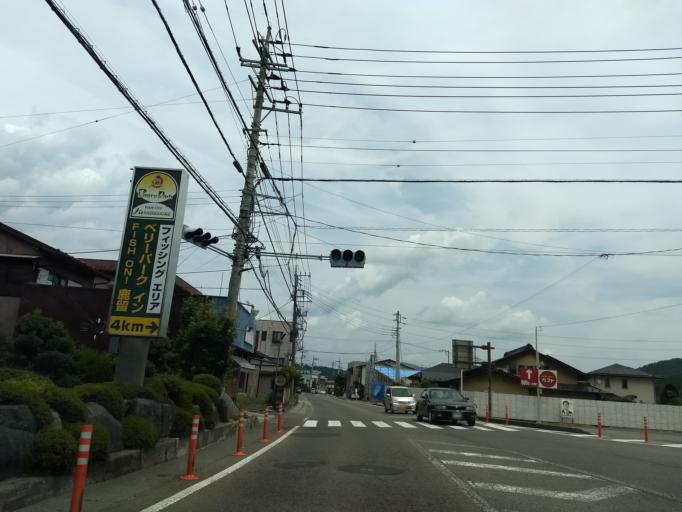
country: JP
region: Yamanashi
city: Otsuki
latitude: 35.5344
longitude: 138.8686
